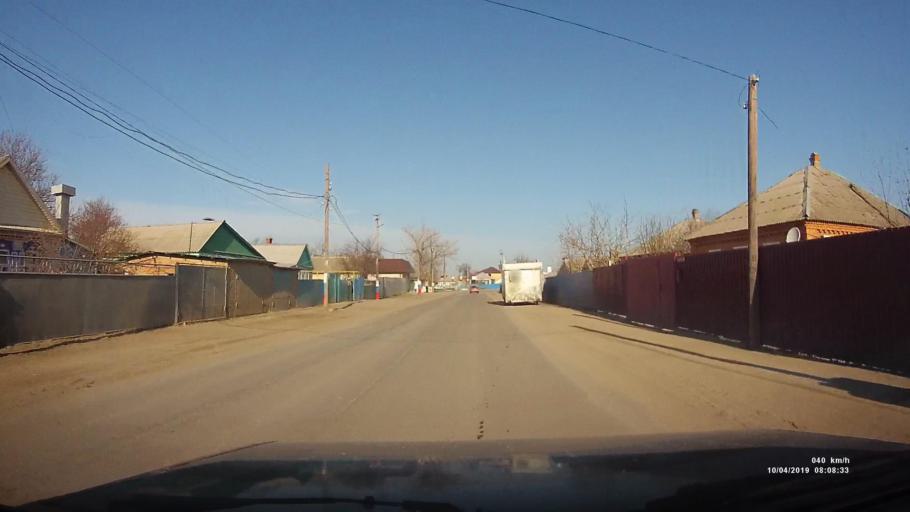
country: RU
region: Rostov
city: Staraya Stanitsa
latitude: 48.3484
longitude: 40.2845
